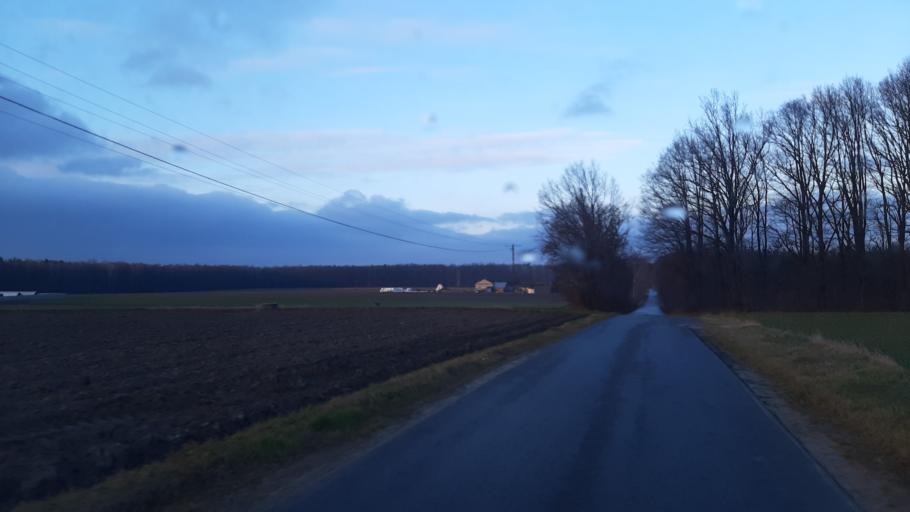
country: PL
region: Lublin Voivodeship
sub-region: Powiat lubelski
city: Garbow
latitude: 51.3678
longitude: 22.3985
